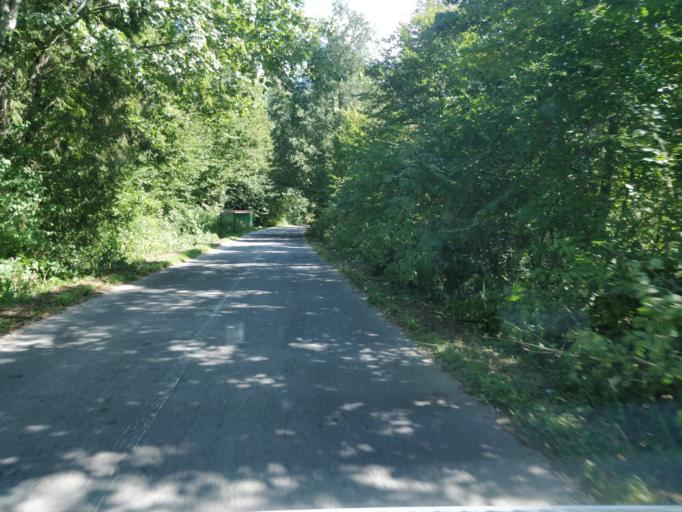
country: RO
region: Cluj
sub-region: Comuna Sacueu
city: Sacuieu
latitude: 46.8533
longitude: 22.8622
